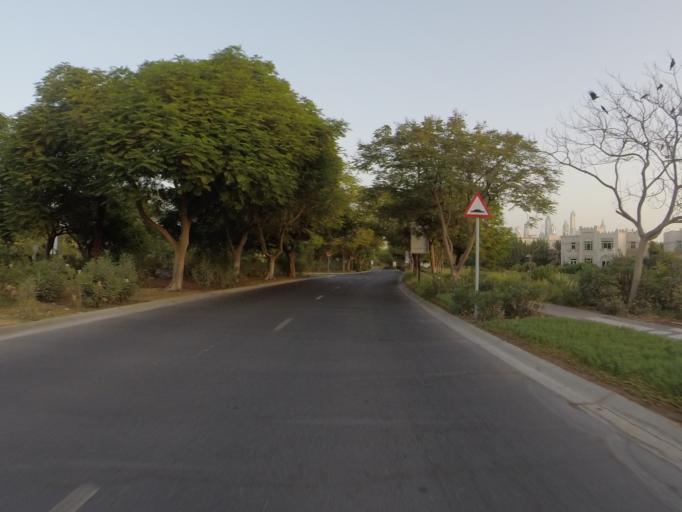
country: AE
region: Dubai
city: Dubai
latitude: 25.0581
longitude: 55.1588
